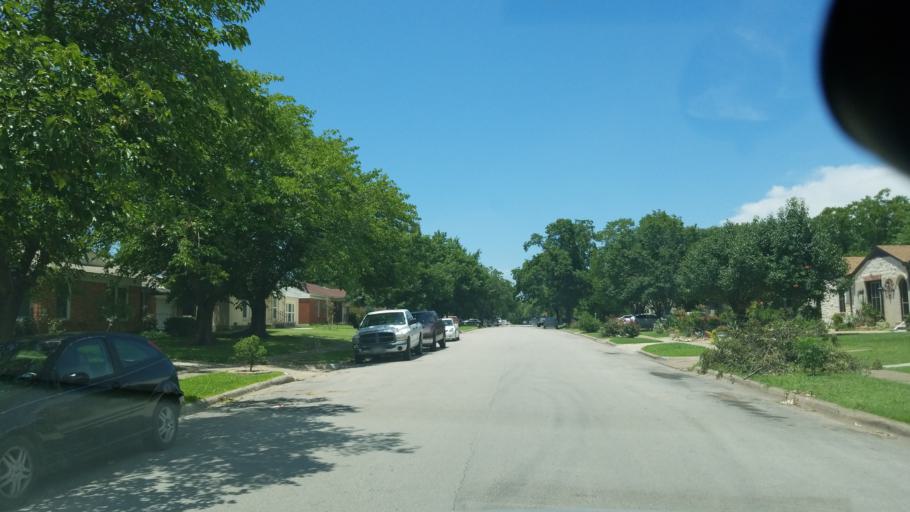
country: US
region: Texas
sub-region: Dallas County
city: Irving
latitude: 32.8294
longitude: -96.9736
